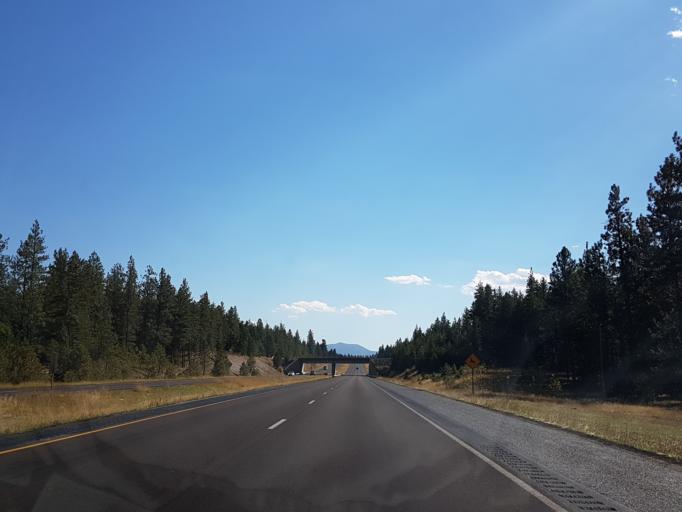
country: US
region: Montana
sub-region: Mineral County
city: Superior
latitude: 47.1292
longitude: -114.7960
